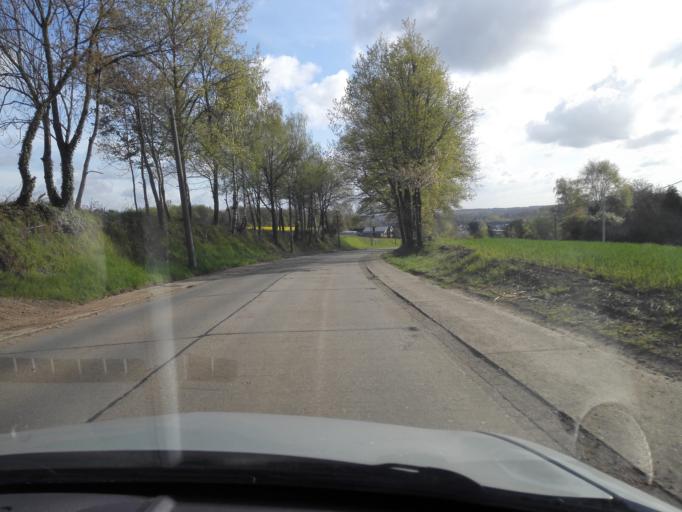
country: BE
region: Flanders
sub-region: Provincie Vlaams-Brabant
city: Aarschot
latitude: 50.9670
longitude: 4.8787
